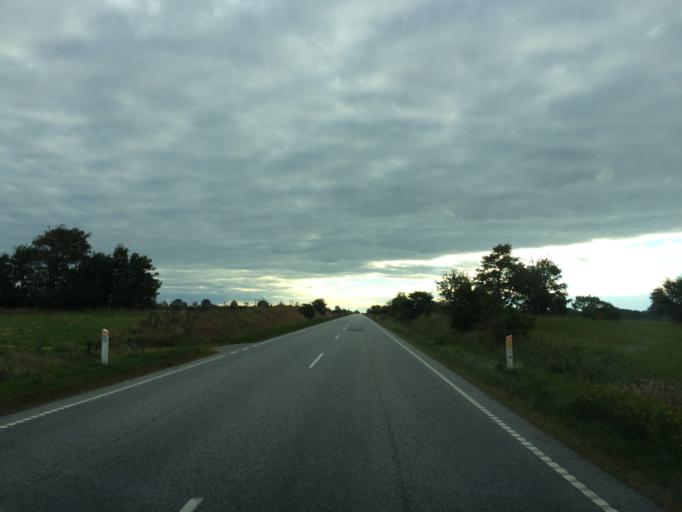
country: DK
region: Central Jutland
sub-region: Ringkobing-Skjern Kommune
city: Tarm
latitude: 55.9677
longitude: 8.5953
